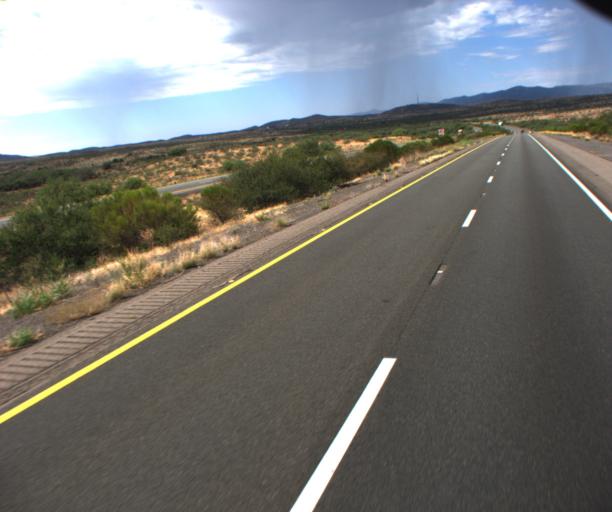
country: US
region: Arizona
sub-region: Yavapai County
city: Spring Valley
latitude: 34.3706
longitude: -112.1111
